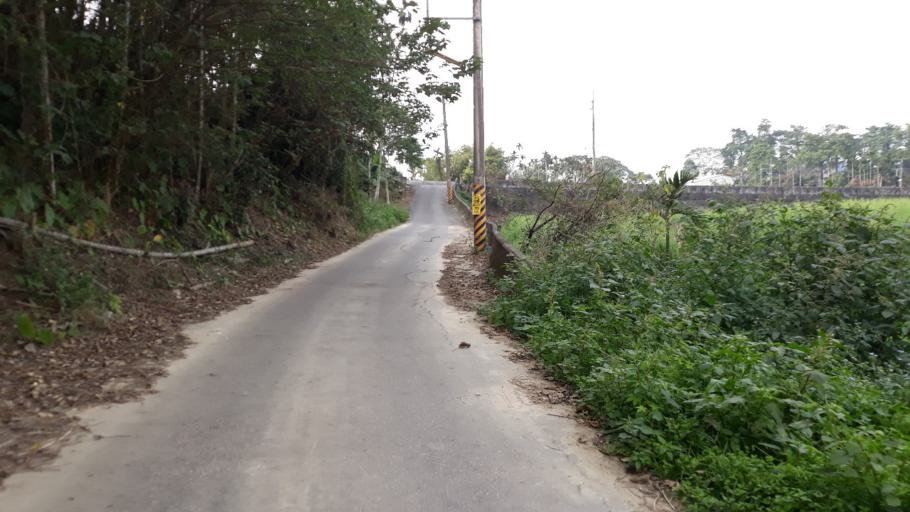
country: TW
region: Taiwan
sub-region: Chiayi
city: Jiayi Shi
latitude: 23.4283
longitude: 120.5241
